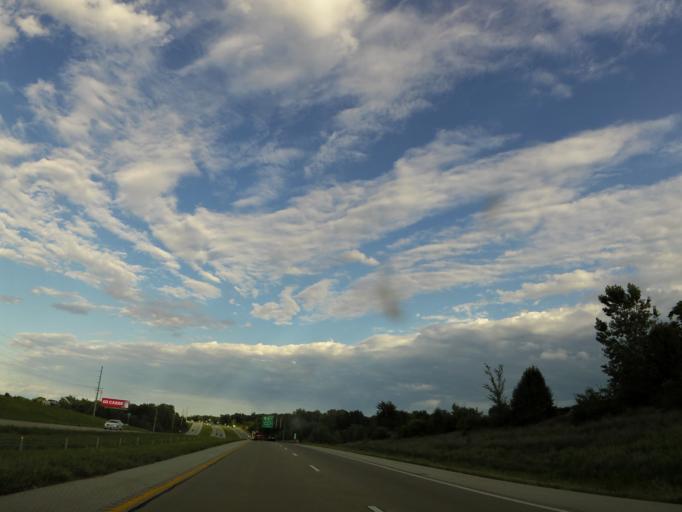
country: US
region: Missouri
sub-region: Saint Charles County
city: Weldon Spring
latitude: 38.7233
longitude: -90.7270
